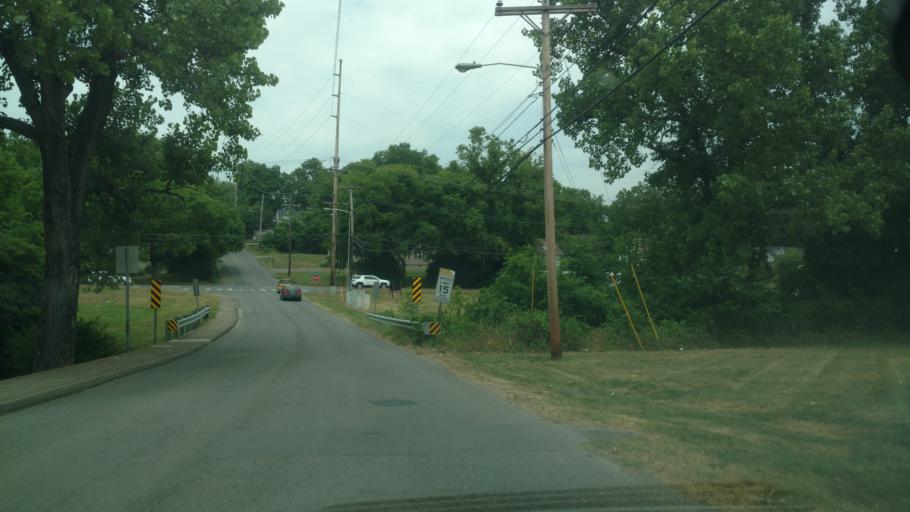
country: US
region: Tennessee
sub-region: Davidson County
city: Nashville
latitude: 36.2072
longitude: -86.7166
